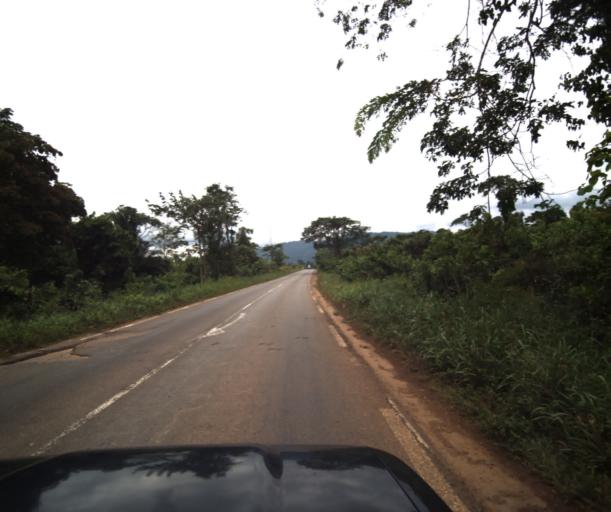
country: CM
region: Centre
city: Eseka
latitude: 3.8773
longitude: 10.8148
